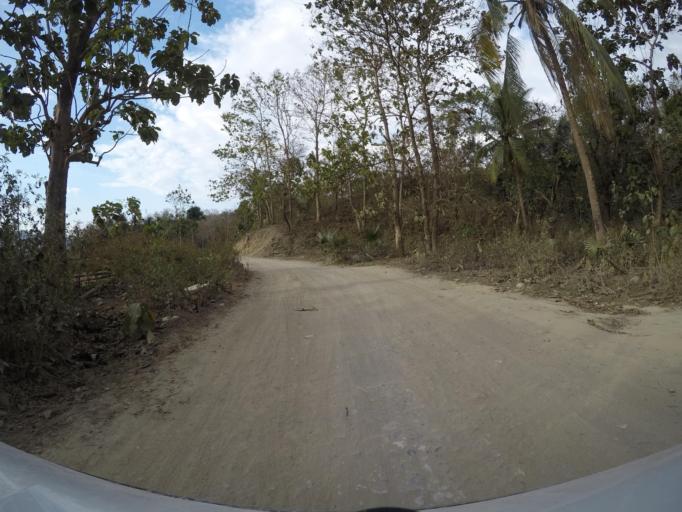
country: TL
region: Bobonaro
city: Maliana
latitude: -8.8894
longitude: 125.2091
